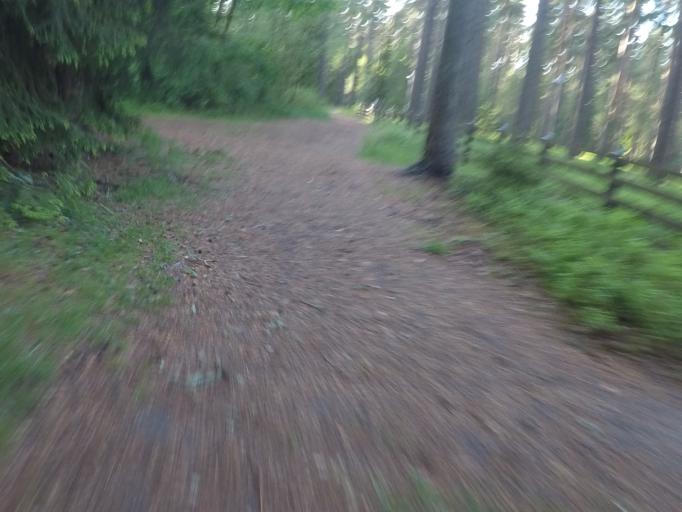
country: SE
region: Soedermanland
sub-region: Eskilstuna Kommun
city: Hallbybrunn
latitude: 59.3965
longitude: 16.4066
